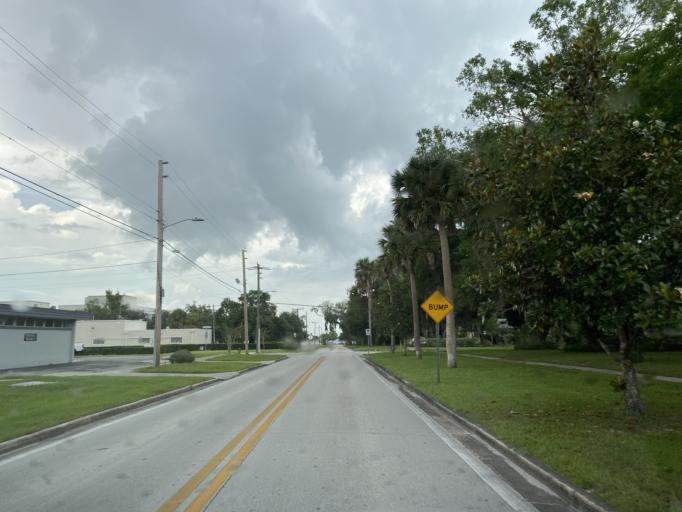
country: US
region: Florida
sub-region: Seminole County
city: Sanford
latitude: 28.8092
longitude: -81.2550
